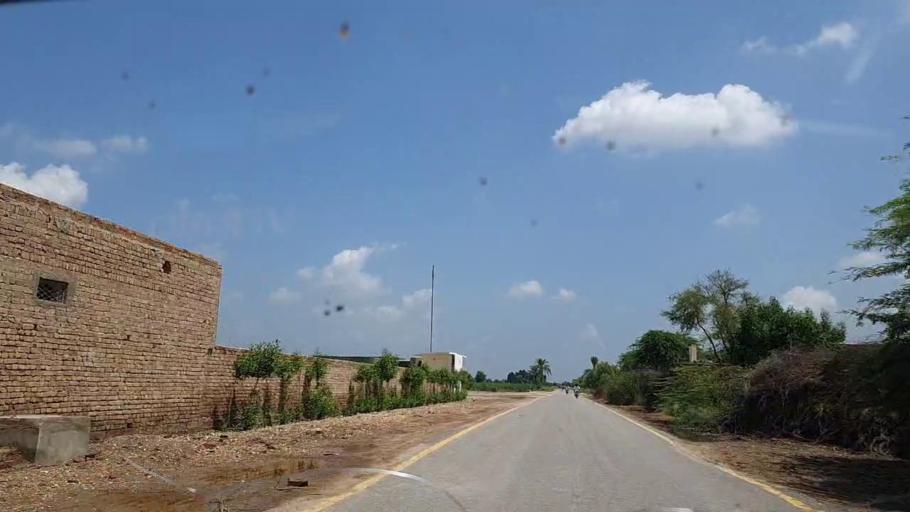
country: PK
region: Sindh
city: Tharu Shah
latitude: 26.9774
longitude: 68.0855
